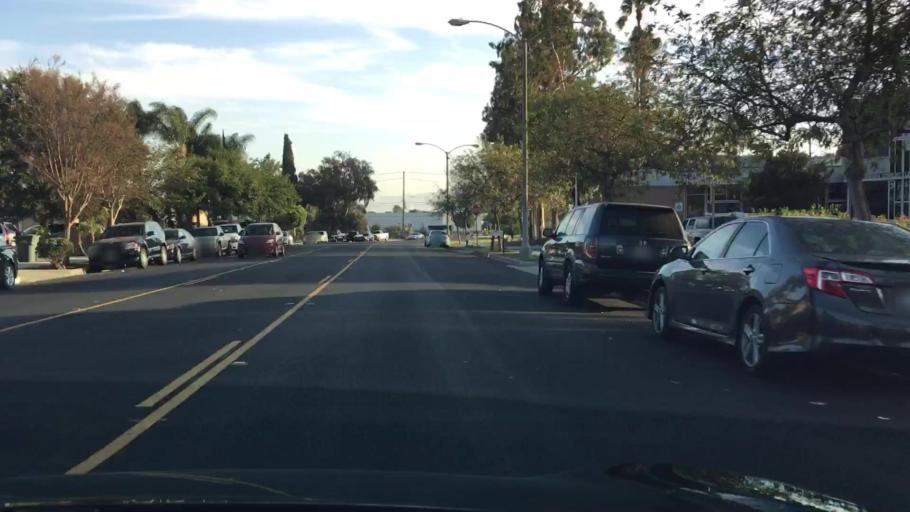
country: US
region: California
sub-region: San Bernardino County
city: Ontario
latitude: 34.0534
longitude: -117.6367
